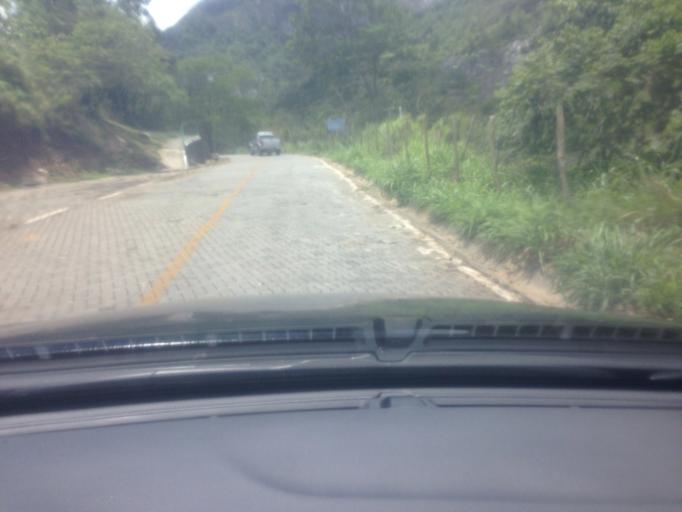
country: BR
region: Espirito Santo
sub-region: Guarapari
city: Guarapari
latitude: -20.6033
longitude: -40.5364
